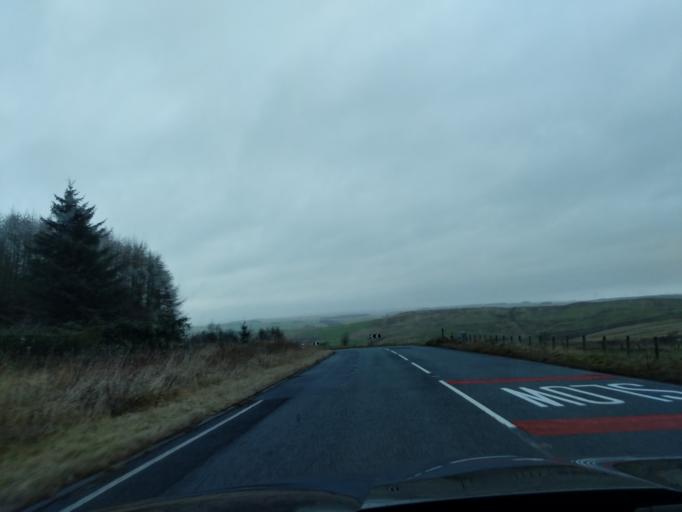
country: GB
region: England
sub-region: Northumberland
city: Otterburn
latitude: 55.2104
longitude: -2.1056
